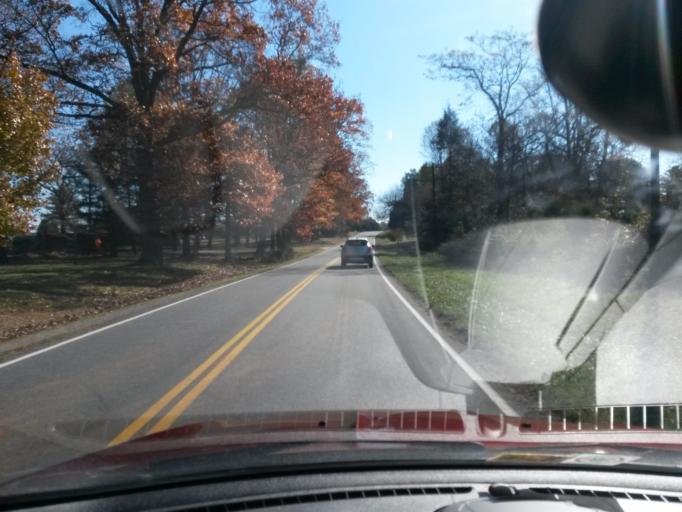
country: US
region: Virginia
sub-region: City of Bedford
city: Bedford
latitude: 37.3767
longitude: -79.5471
